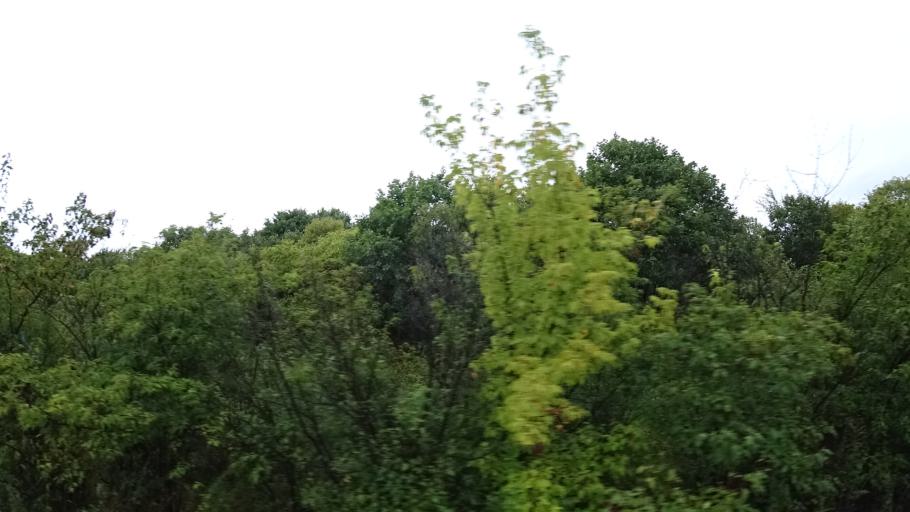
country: RU
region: Primorskiy
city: Monastyrishche
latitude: 44.2636
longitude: 132.4235
